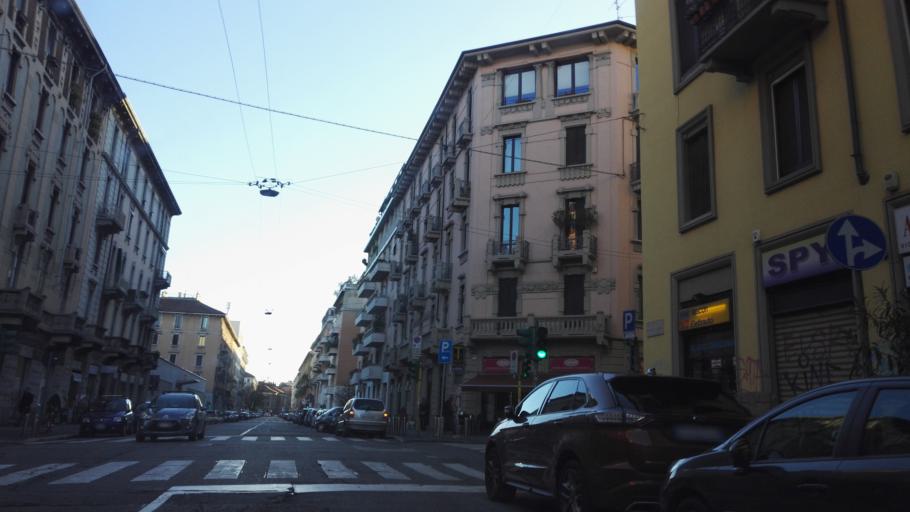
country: IT
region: Lombardy
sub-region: Citta metropolitana di Milano
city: Milano
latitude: 45.4652
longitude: 9.2113
